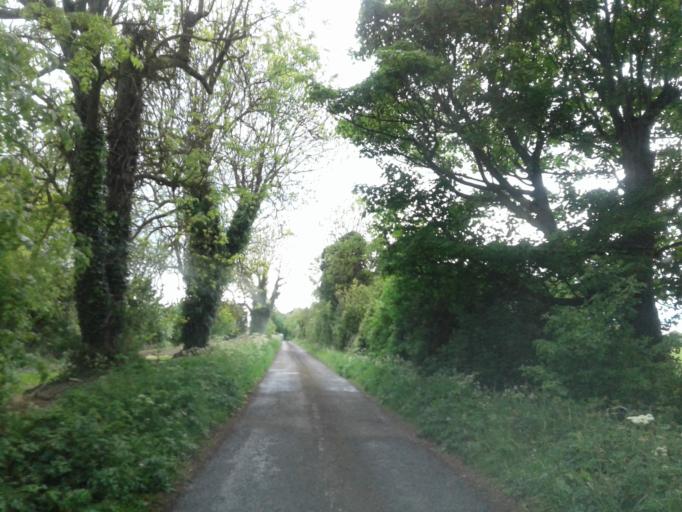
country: IE
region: Leinster
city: Ballymun
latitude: 53.4258
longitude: -6.2742
